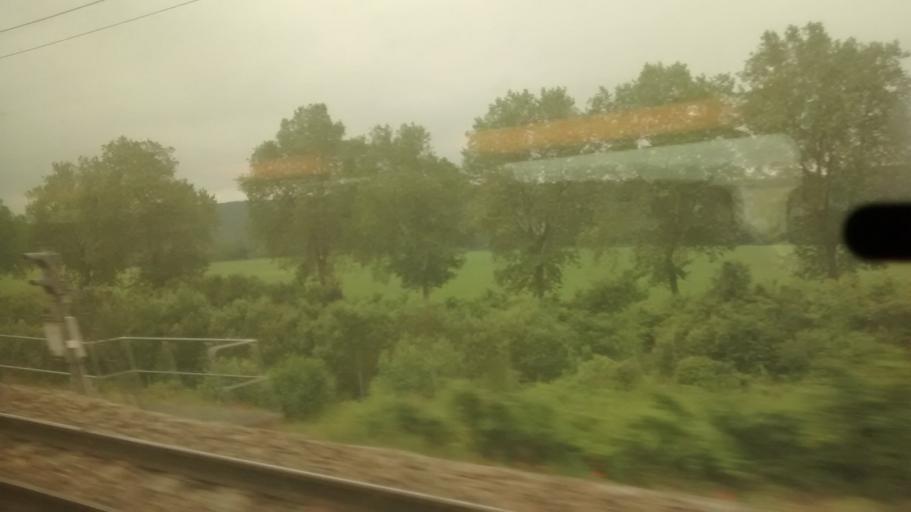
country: FR
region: Bourgogne
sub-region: Departement de l'Yonne
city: Malay-le-Grand
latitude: 48.1775
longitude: 3.3575
